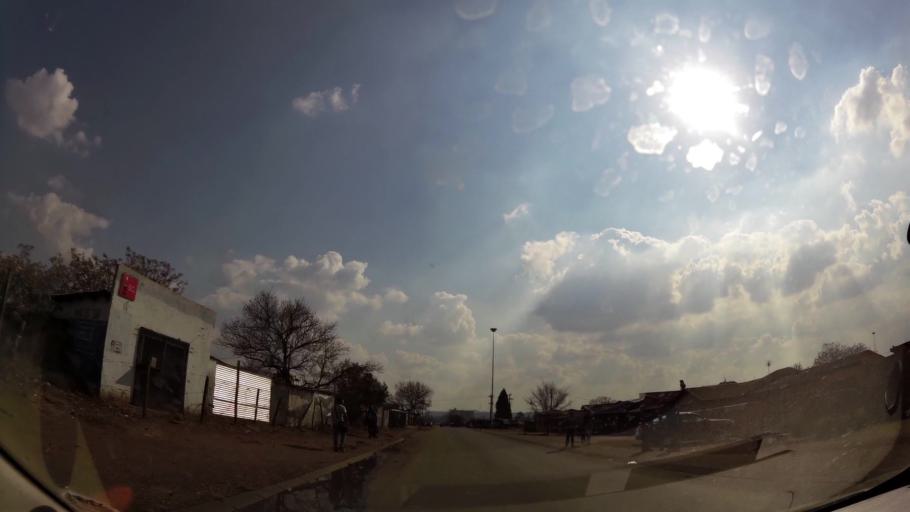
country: ZA
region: Gauteng
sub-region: Ekurhuleni Metropolitan Municipality
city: Germiston
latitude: -26.3087
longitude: 28.1500
